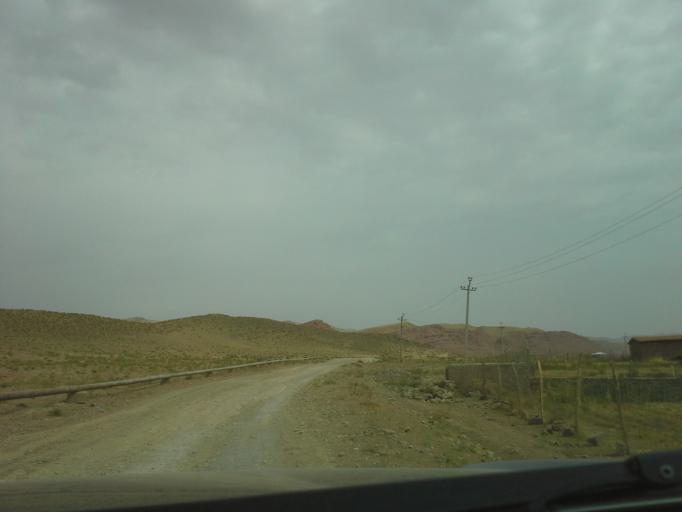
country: UZ
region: Qashqadaryo
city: Qorashina
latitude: 37.9319
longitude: 66.4988
